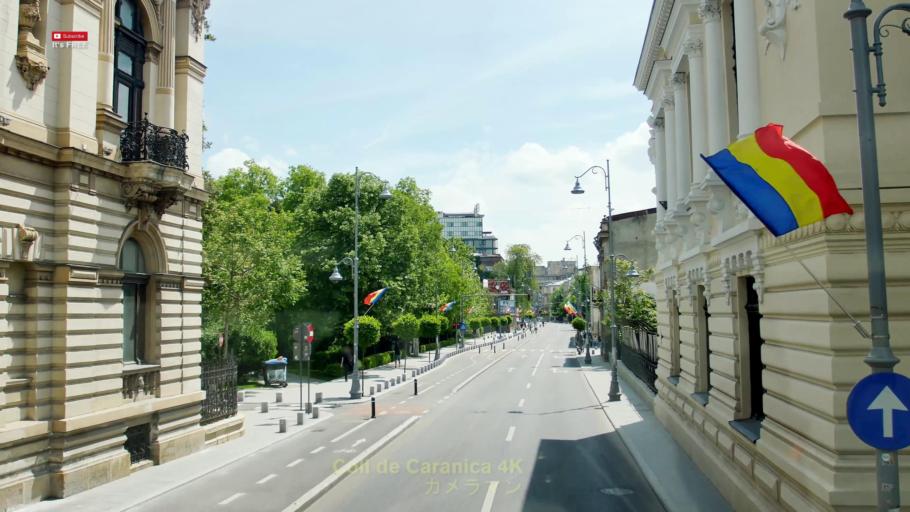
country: RO
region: Bucuresti
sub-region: Municipiul Bucuresti
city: Bucuresti
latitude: 44.4479
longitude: 26.0894
